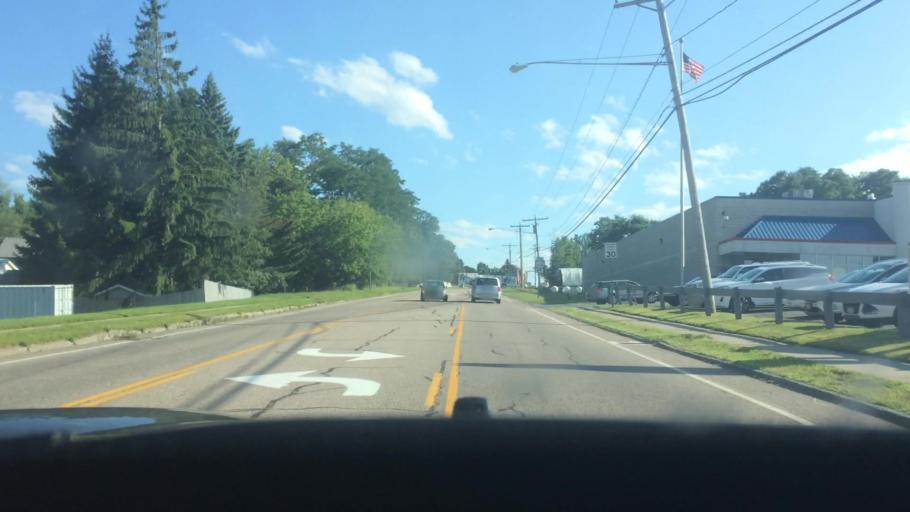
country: US
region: New York
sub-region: Franklin County
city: Malone
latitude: 44.8469
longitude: -74.3008
